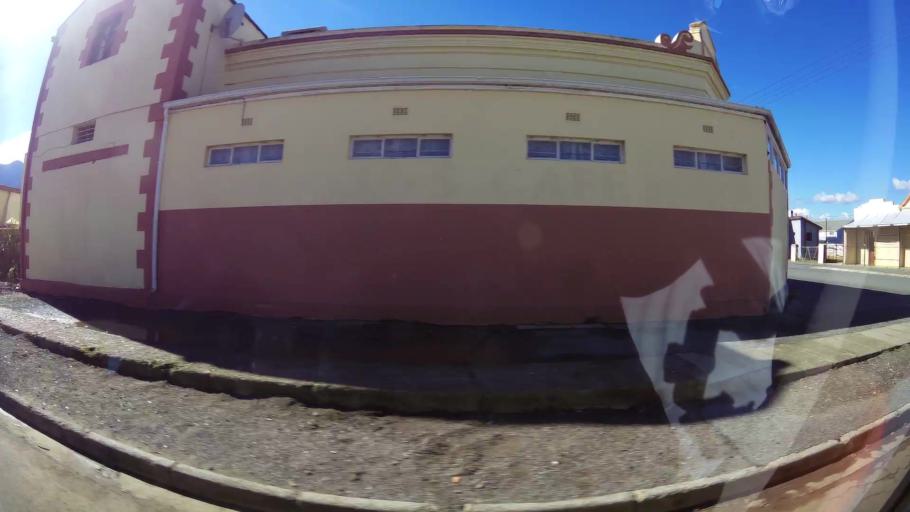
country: ZA
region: Western Cape
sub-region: Cape Winelands District Municipality
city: Ashton
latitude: -33.7962
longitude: 19.8836
